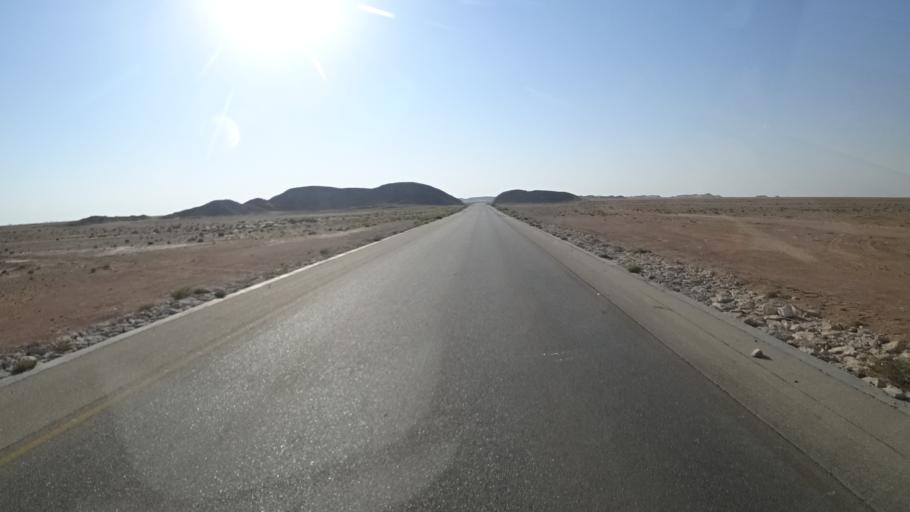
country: OM
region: Zufar
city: Salalah
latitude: 17.6394
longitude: 53.8936
